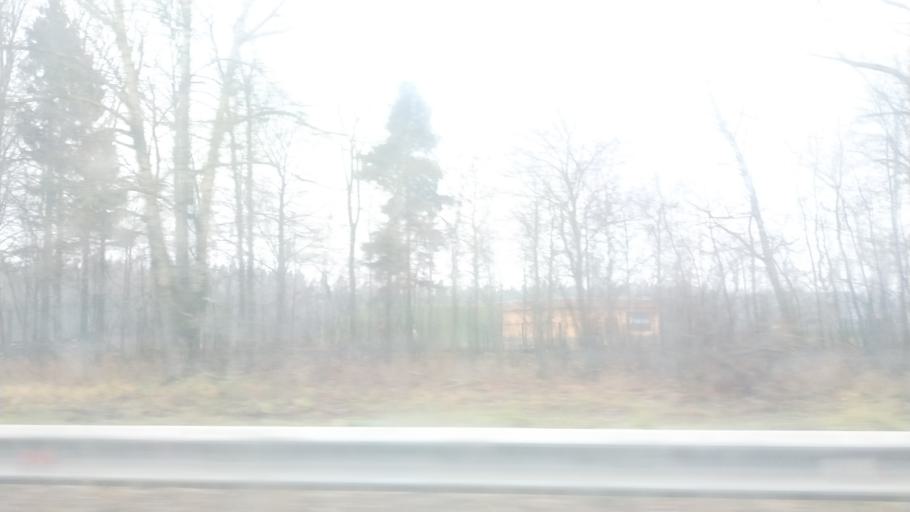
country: RU
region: Moskovskaya
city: Marfino
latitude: 56.0421
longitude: 37.5409
